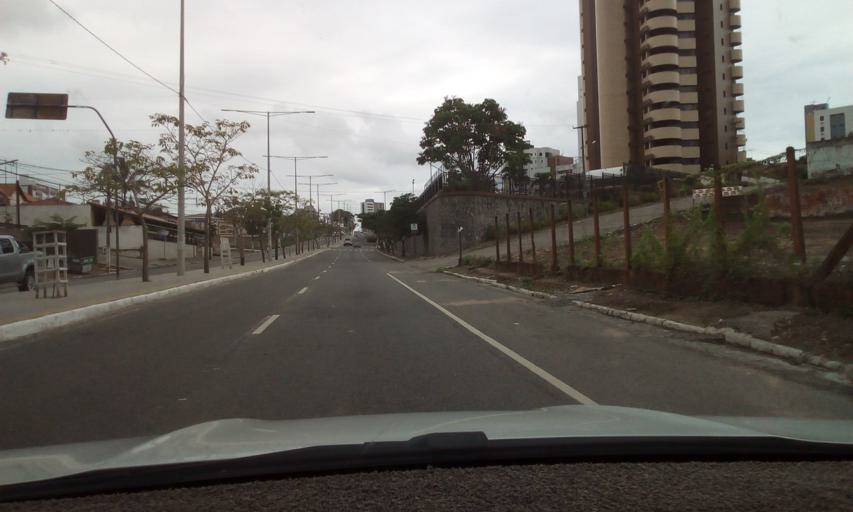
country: BR
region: Paraiba
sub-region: Campina Grande
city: Campina Grande
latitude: -7.2127
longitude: -35.8768
